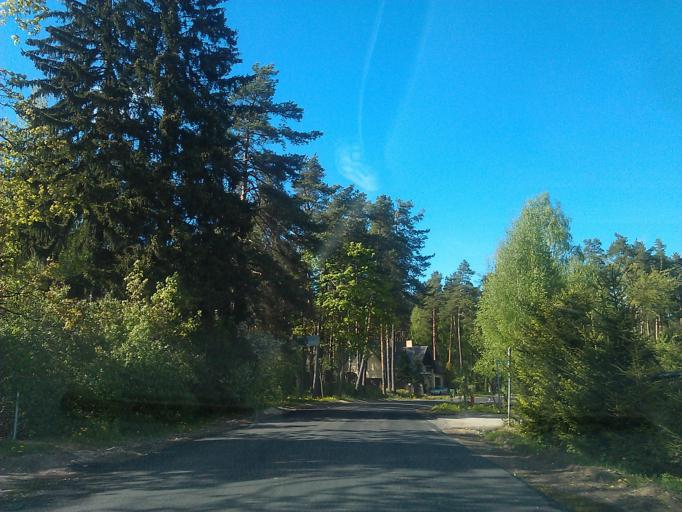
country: LV
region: Riga
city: Bergi
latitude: 57.0145
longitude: 24.2594
